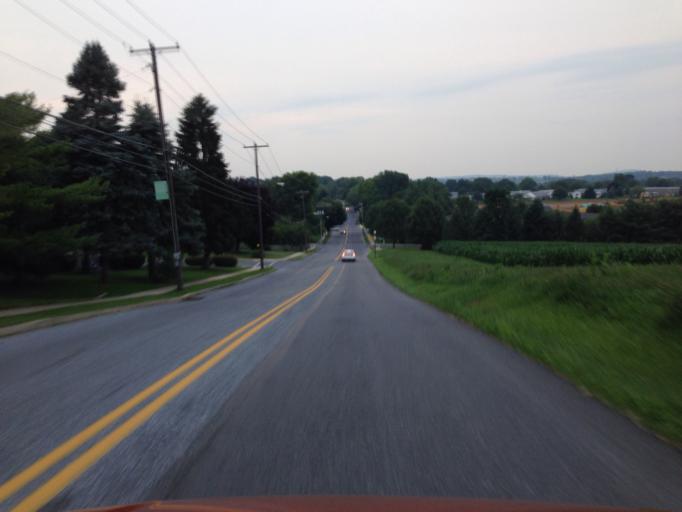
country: US
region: Pennsylvania
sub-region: Lancaster County
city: Lititz
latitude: 40.1452
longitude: -76.2940
